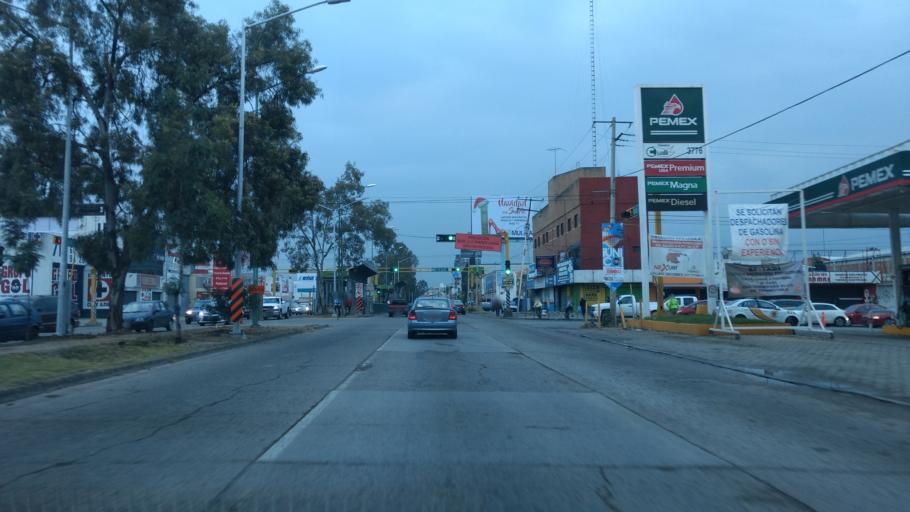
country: MX
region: Guanajuato
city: Leon
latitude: 21.0972
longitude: -101.6554
